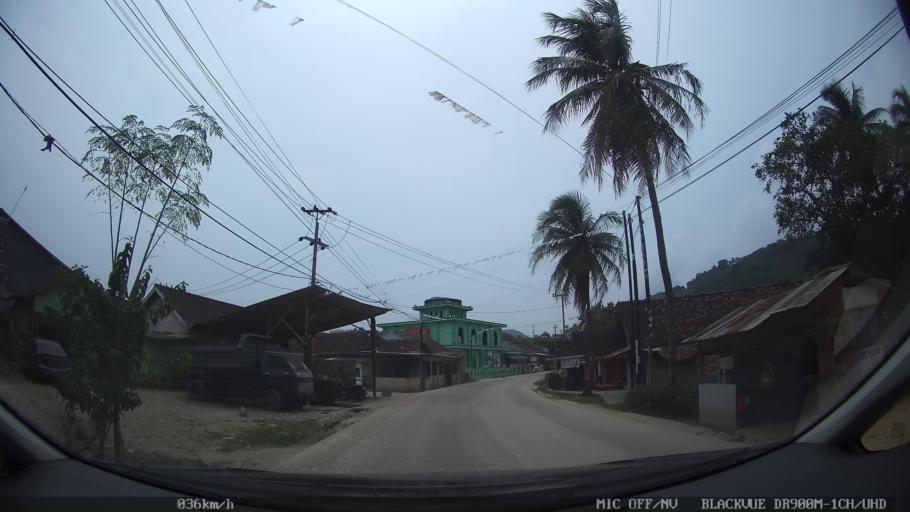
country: ID
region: Lampung
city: Bandarlampung
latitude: -5.4064
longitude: 105.3088
